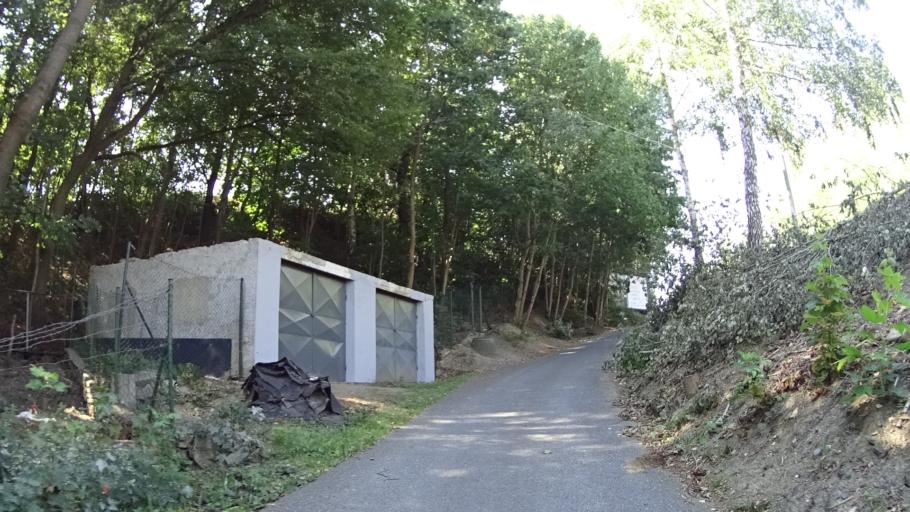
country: CZ
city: Straz nad Nisou
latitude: 50.7780
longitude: 15.0392
